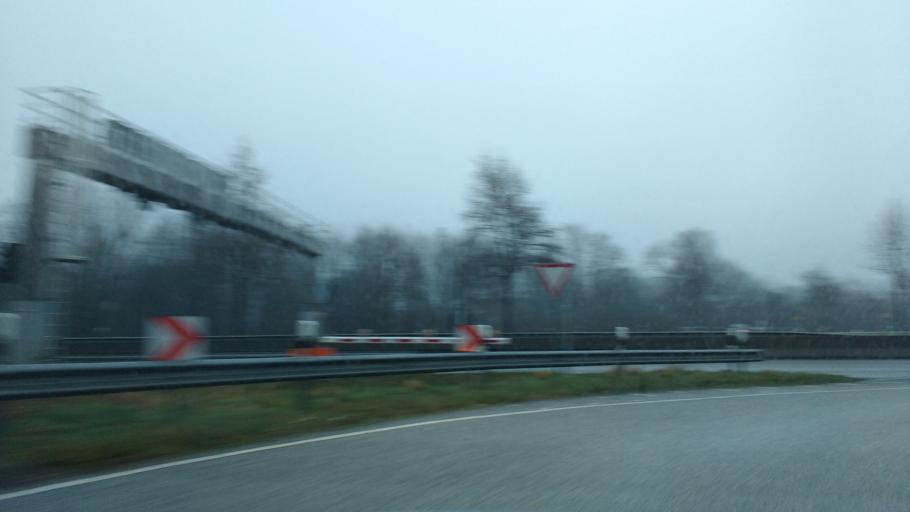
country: DE
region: Schleswig-Holstein
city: Westerronfeld
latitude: 54.2963
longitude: 9.6533
